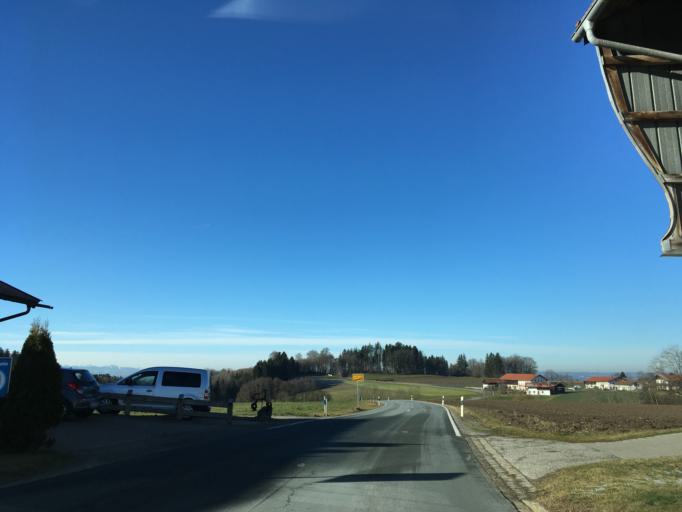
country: DE
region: Bavaria
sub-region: Upper Bavaria
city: Amerang
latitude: 47.9908
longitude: 12.3323
